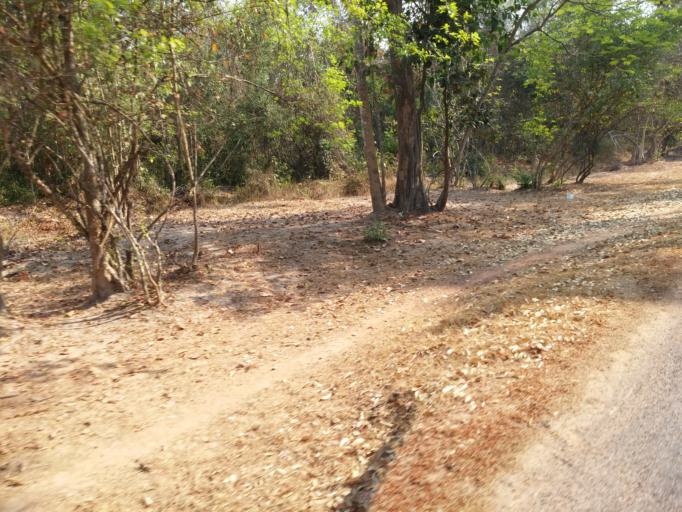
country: KH
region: Siem Reap
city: Siem Reap
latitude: 13.4165
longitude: 103.8907
